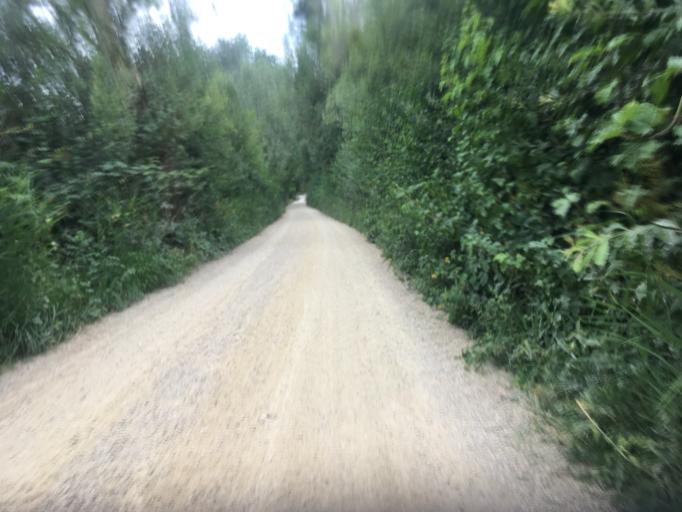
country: CH
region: Bern
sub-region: Seeland District
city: Erlach
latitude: 47.0473
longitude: 7.1031
